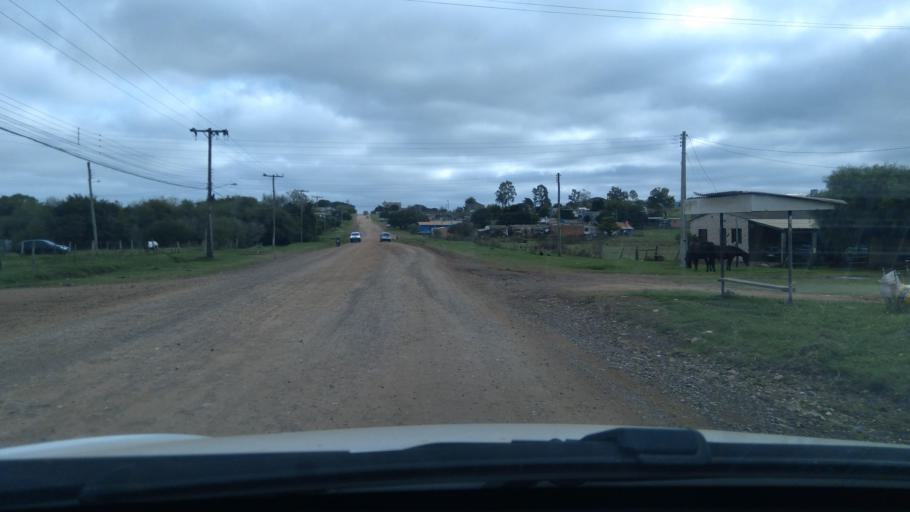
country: BR
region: Rio Grande do Sul
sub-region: Dom Pedrito
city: Dom Pedrito
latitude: -30.9817
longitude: -54.6521
